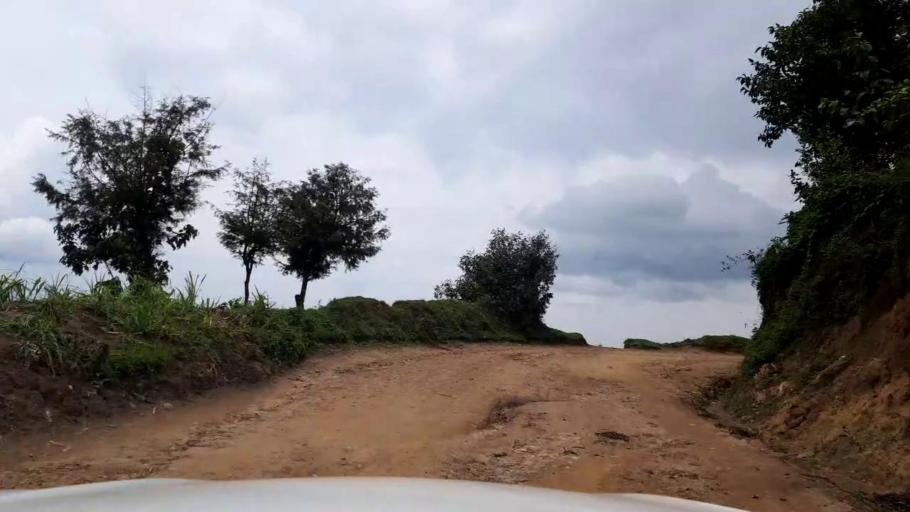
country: RW
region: Western Province
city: Kibuye
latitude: -1.9620
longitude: 29.3940
